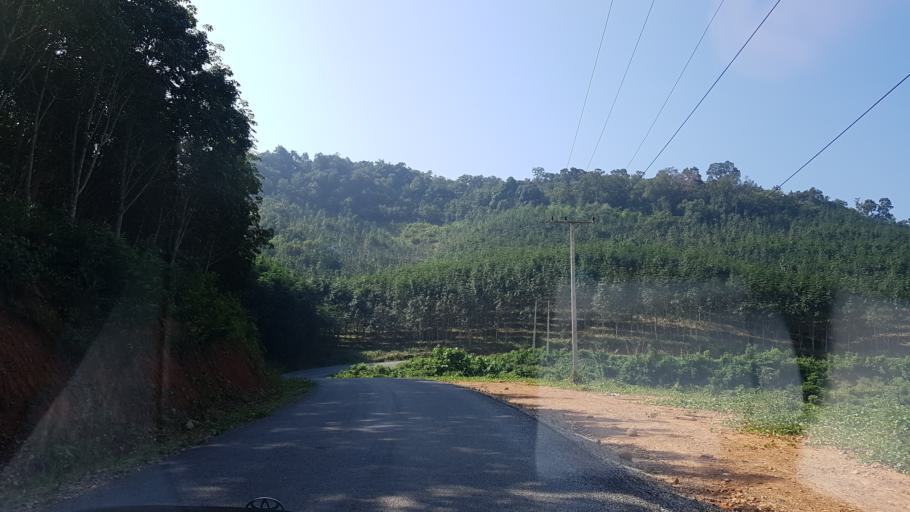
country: LA
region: Oudomxai
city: Muang Xay
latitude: 20.7132
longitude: 102.0729
